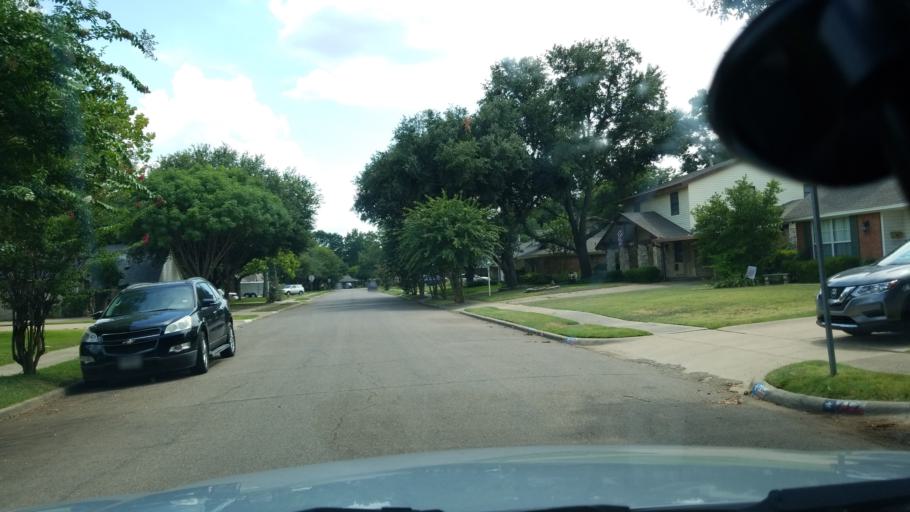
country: US
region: Texas
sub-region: Dallas County
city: Irving
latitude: 32.8237
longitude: -96.9802
